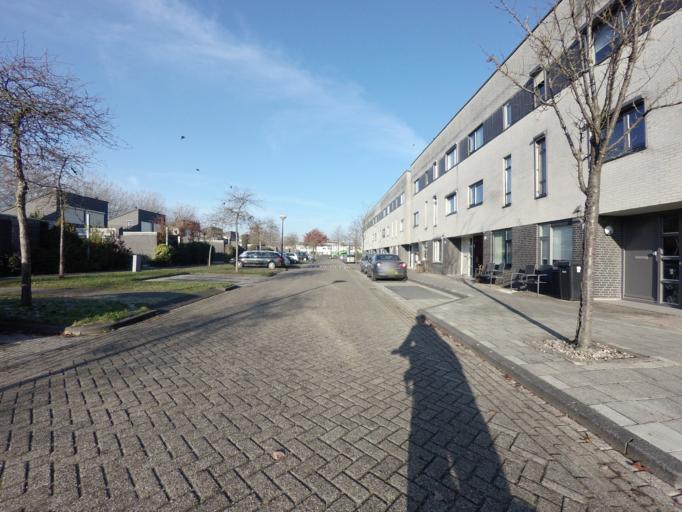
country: NL
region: Utrecht
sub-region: Gemeente Woerden
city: Woerden
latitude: 52.0792
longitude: 4.8999
